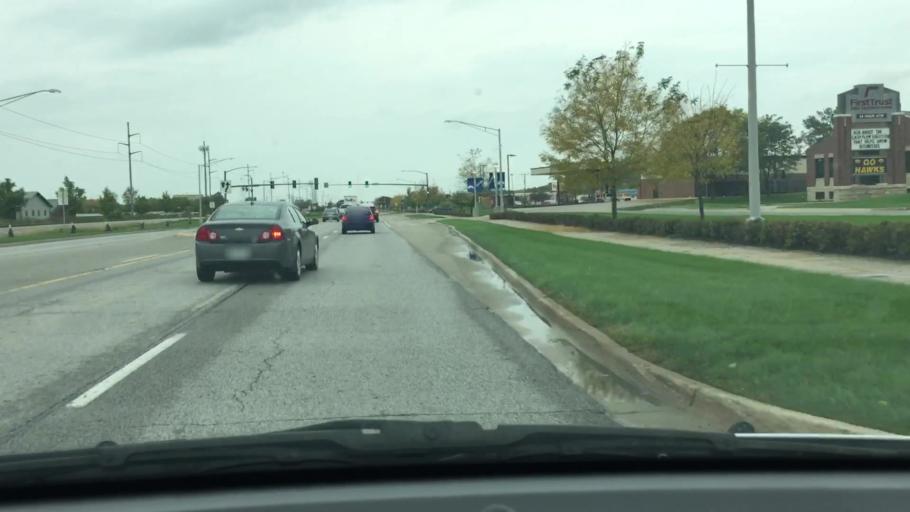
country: US
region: Iowa
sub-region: Johnson County
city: Coralville
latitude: 41.6787
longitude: -91.5898
